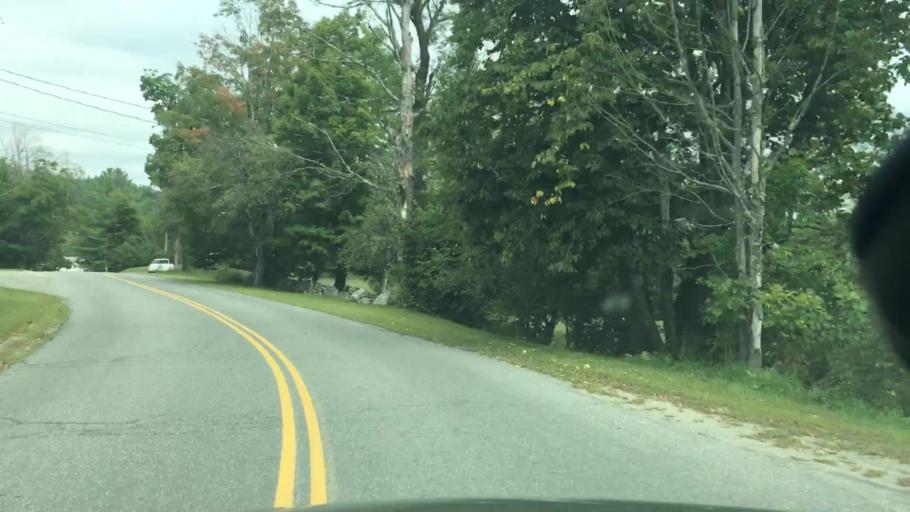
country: US
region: Massachusetts
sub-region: Franklin County
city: Colrain
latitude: 42.7845
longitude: -72.7680
